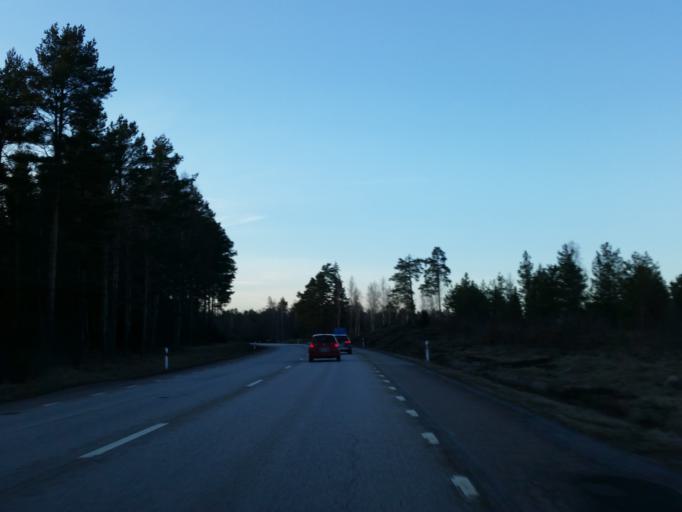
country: SE
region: Kalmar
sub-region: Oskarshamns Kommun
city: Oskarshamn
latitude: 57.4896
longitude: 16.5180
